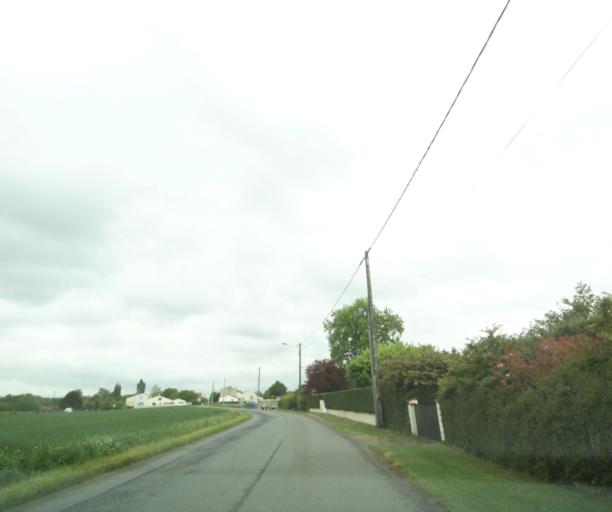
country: FR
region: Poitou-Charentes
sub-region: Departement de la Charente-Maritime
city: Chaniers
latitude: 45.6966
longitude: -0.5230
